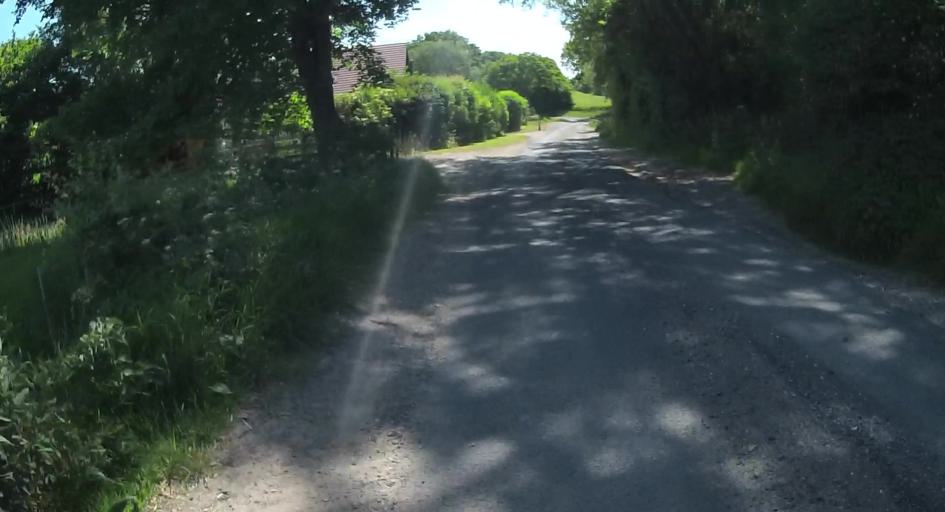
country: GB
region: England
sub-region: Hampshire
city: Kingsclere
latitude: 51.3291
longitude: -1.2889
